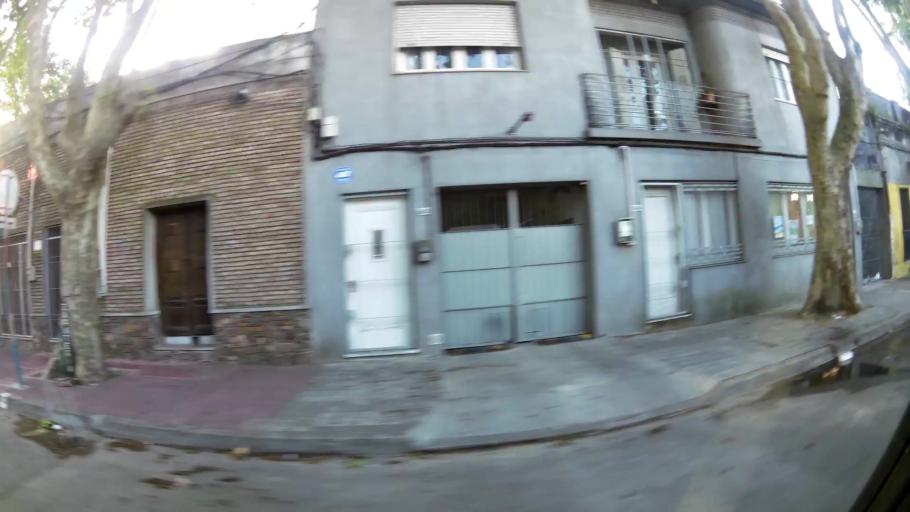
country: UY
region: Montevideo
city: Montevideo
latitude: -34.8774
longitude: -56.1412
